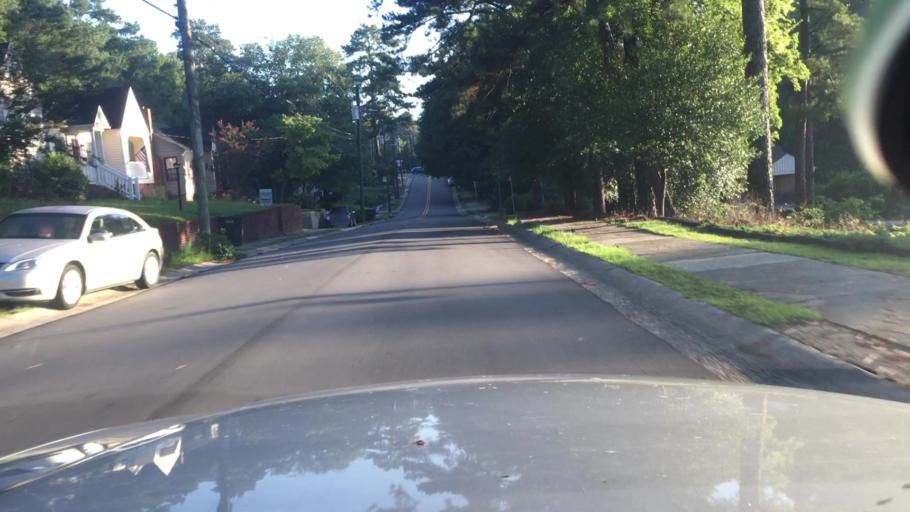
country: US
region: North Carolina
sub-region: Cumberland County
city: Fayetteville
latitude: 35.0669
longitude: -78.9069
